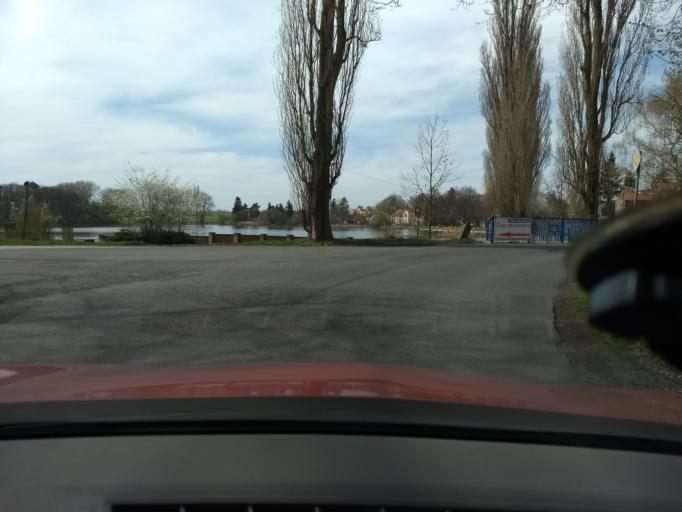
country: CZ
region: Central Bohemia
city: Hostivice
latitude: 50.0691
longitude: 14.2473
